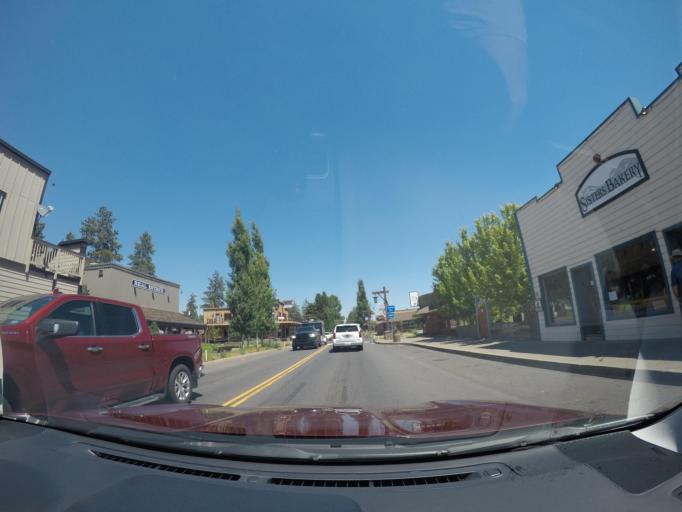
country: US
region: Oregon
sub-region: Deschutes County
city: Sisters
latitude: 44.2913
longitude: -121.5481
